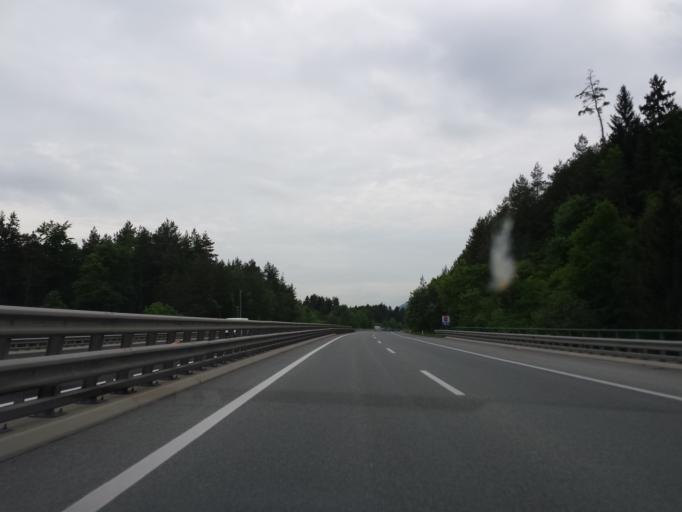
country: AT
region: Lower Austria
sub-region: Politischer Bezirk Neunkirchen
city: Seebenstein
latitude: 47.6973
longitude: 16.1305
